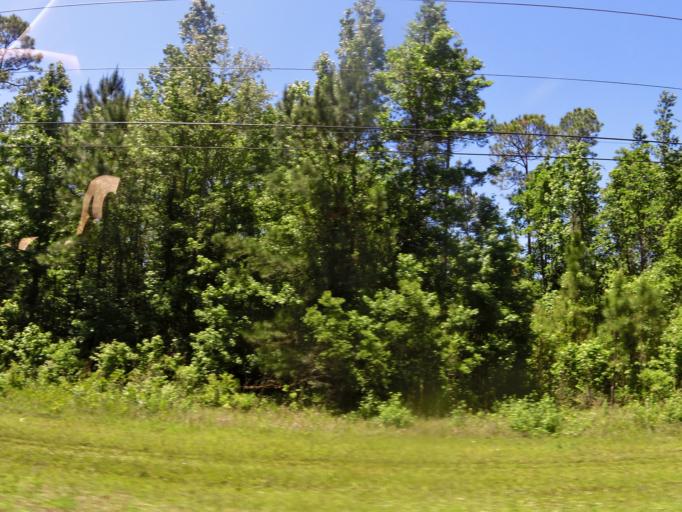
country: US
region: Florida
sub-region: Saint Johns County
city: Fruit Cove
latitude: 30.0430
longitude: -81.5801
